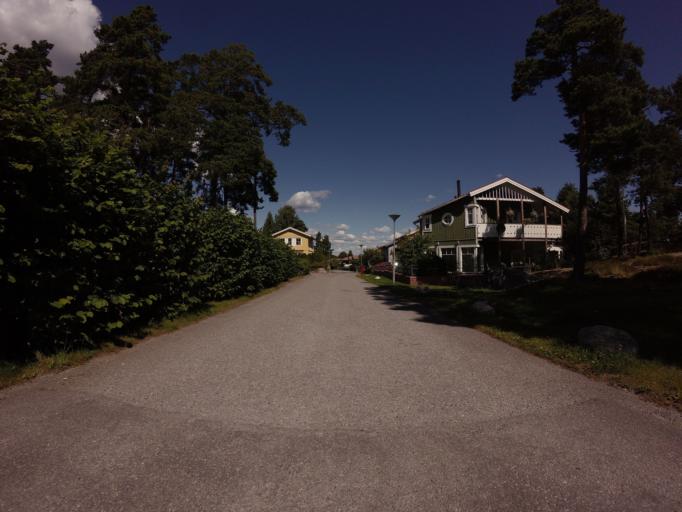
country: SE
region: Stockholm
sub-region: Jarfalla Kommun
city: Jakobsberg
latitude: 59.4605
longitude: 17.8843
